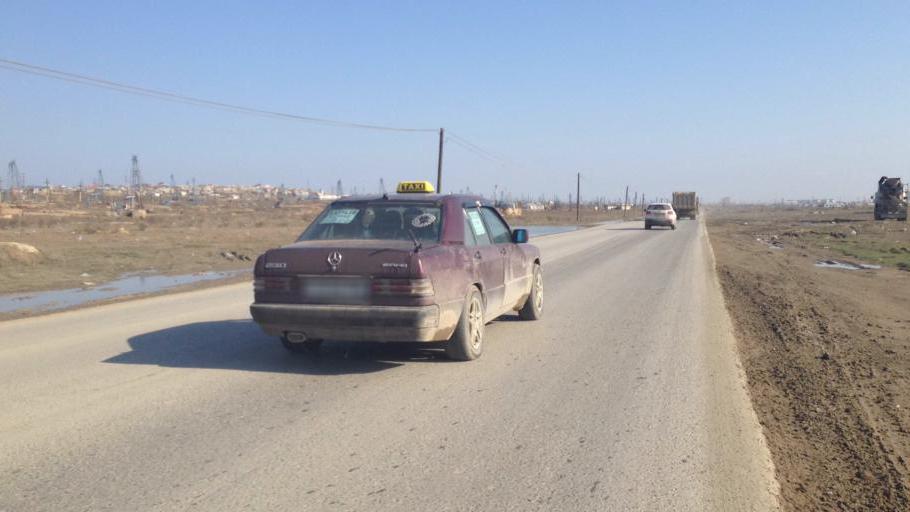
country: AZ
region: Baki
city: Balakhani
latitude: 40.4529
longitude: 49.8956
